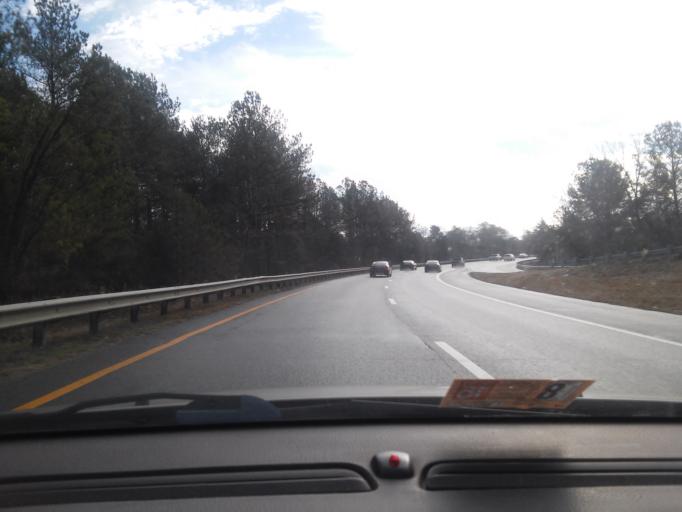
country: US
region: Virginia
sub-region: Henrico County
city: Lakeside
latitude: 37.5861
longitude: -77.4719
